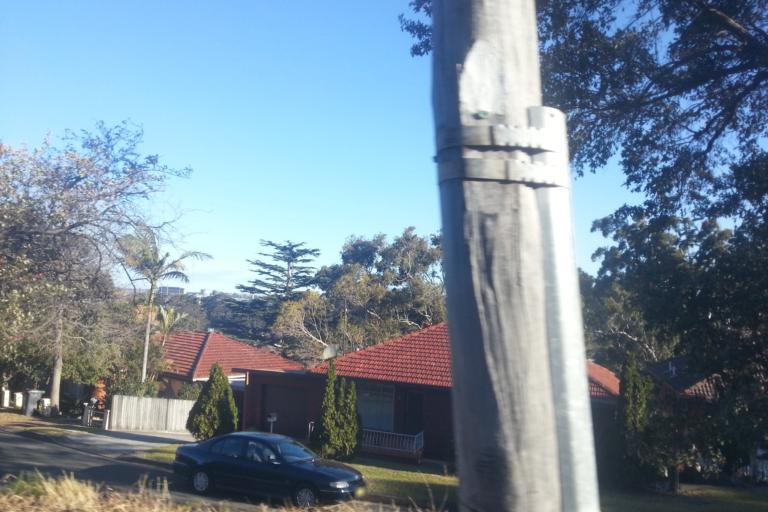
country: AU
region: New South Wales
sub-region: Wollongong
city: Mangerton
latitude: -34.4342
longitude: 150.8781
